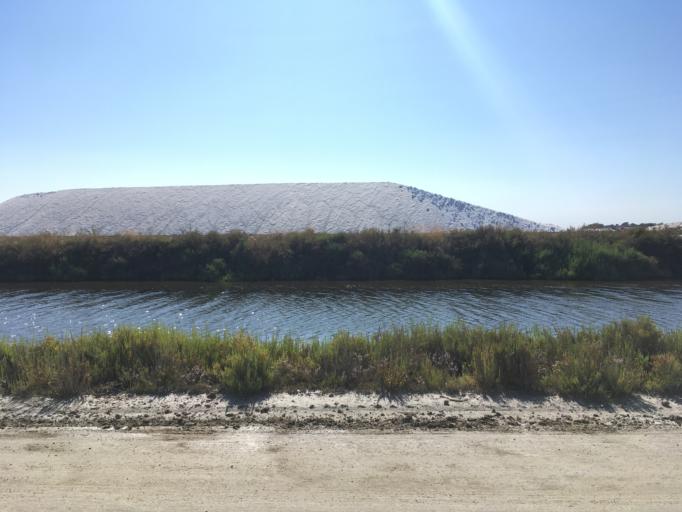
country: FR
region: Languedoc-Roussillon
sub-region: Departement du Gard
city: Aigues-Mortes
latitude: 43.5490
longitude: 4.1870
